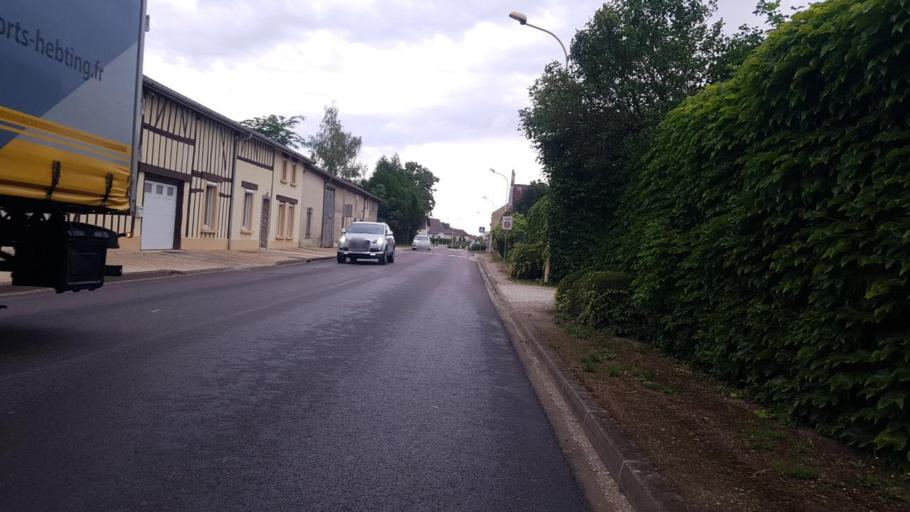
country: FR
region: Champagne-Ardenne
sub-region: Departement de la Marne
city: Vitry-le-Francois
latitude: 48.7506
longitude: 4.7043
